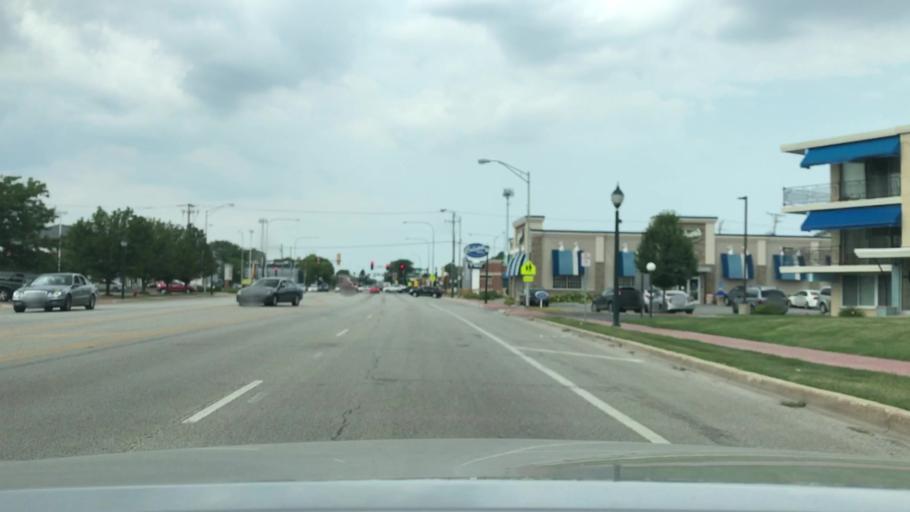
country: US
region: Illinois
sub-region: Cook County
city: Evergreen Park
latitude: 41.7192
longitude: -87.7018
